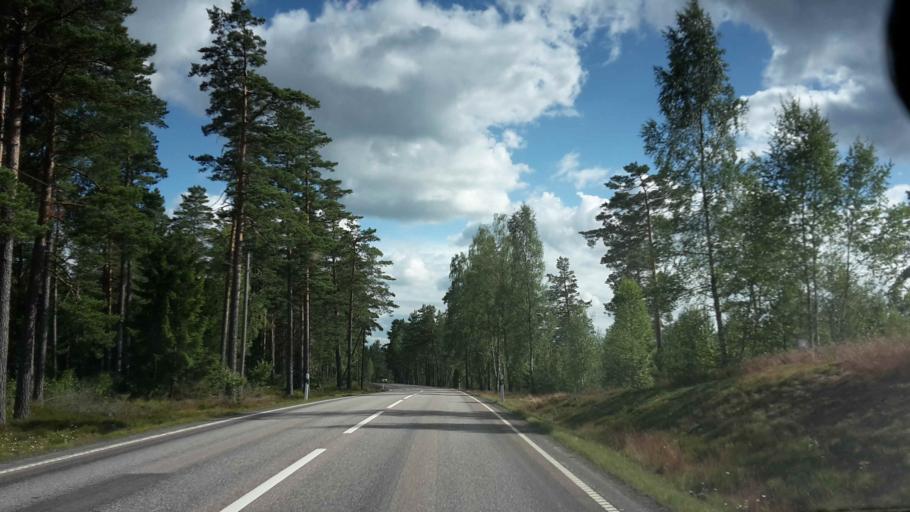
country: SE
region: OErebro
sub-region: Hallsbergs Kommun
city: Palsboda
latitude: 58.8476
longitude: 15.4042
